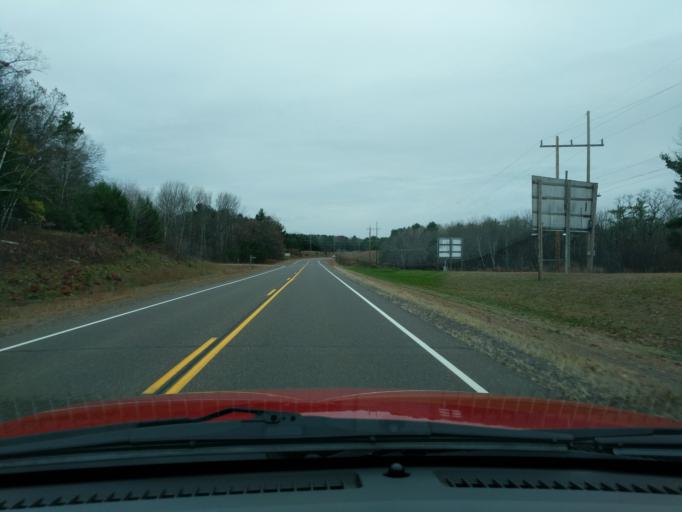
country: US
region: Wisconsin
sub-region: Burnett County
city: Siren
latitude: 45.8089
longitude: -92.2135
